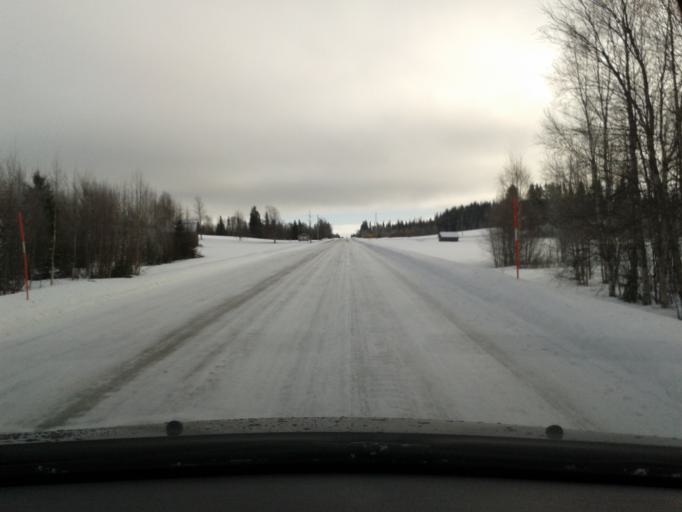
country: SE
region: Vaesterbotten
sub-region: Vilhelmina Kommun
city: Sjoberg
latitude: 64.7906
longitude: 16.0946
